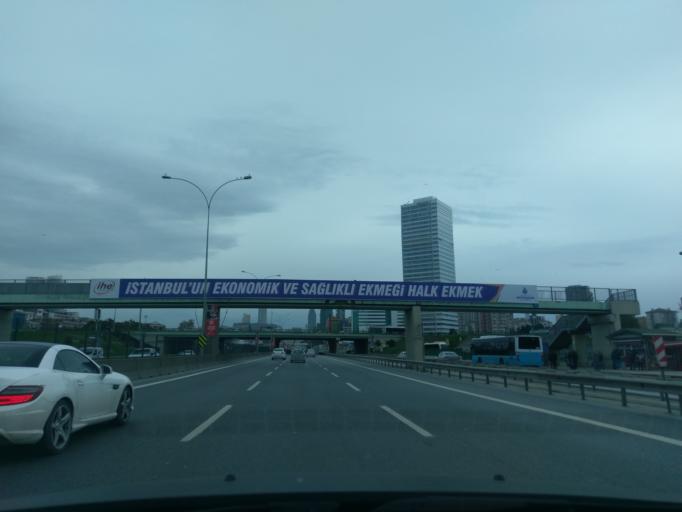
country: TR
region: Istanbul
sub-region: Atasehir
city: Atasehir
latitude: 40.9932
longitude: 29.0713
